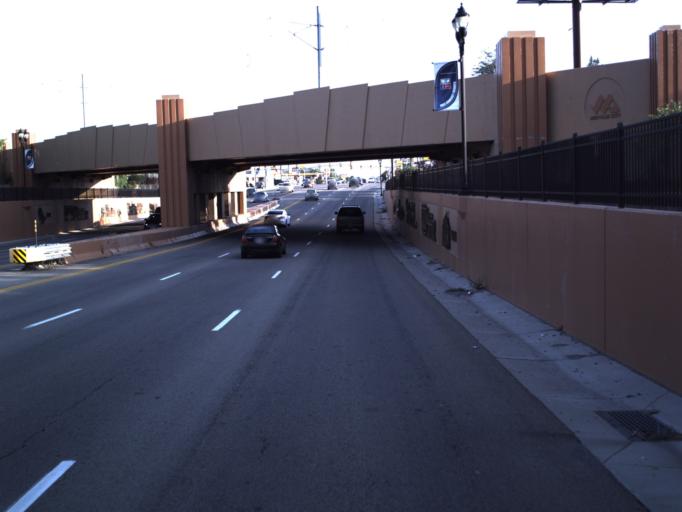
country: US
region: Utah
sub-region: Salt Lake County
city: Midvale
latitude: 40.6088
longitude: -111.8908
